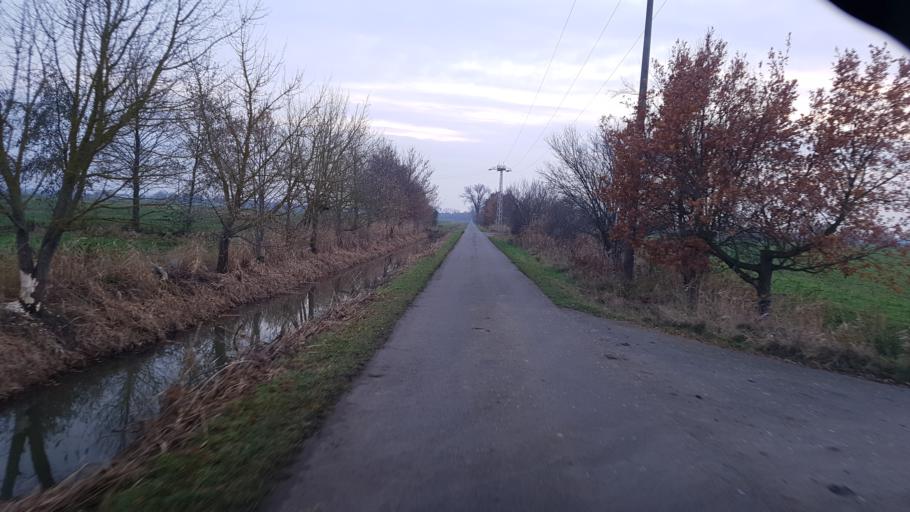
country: DE
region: Brandenburg
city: Ziltendorf
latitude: 52.2372
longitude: 14.6632
